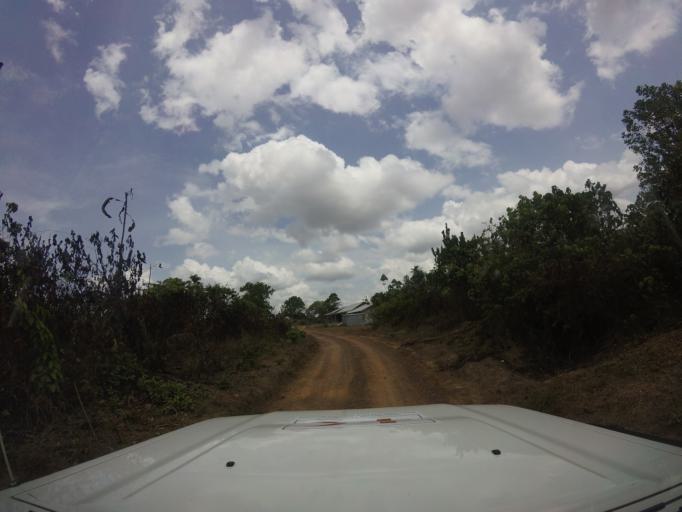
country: LR
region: Bomi
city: Tubmanburg
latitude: 6.8577
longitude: -10.8184
